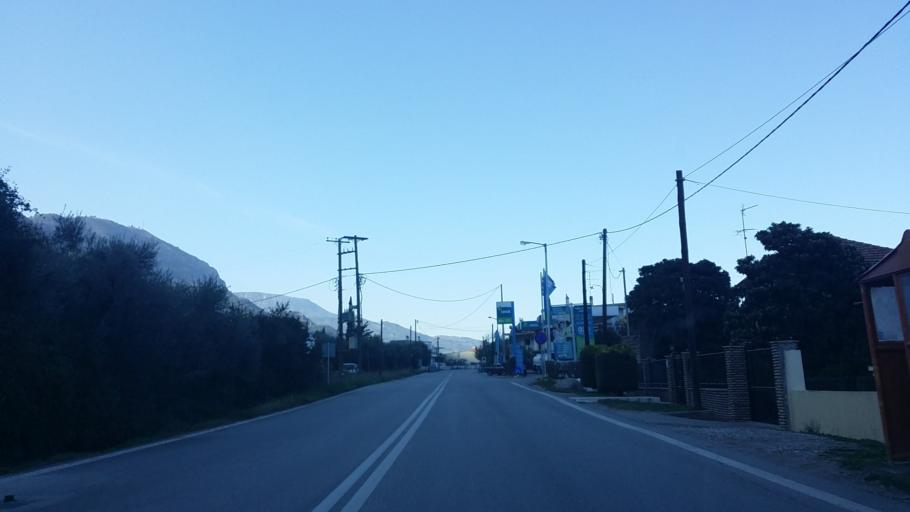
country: GR
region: West Greece
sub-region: Nomos Achaias
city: Temeni
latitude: 38.1836
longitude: 22.2032
